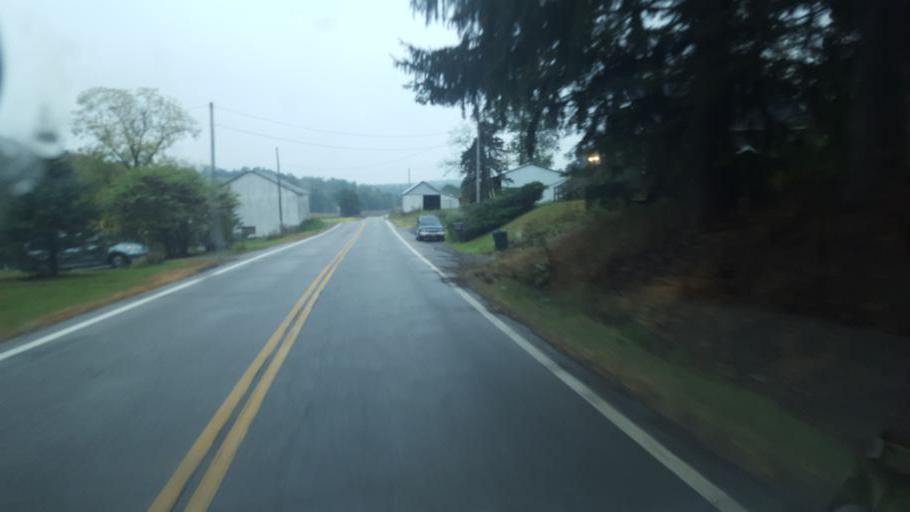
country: US
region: Ohio
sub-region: Sandusky County
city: Bellville
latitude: 40.5820
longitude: -82.3957
